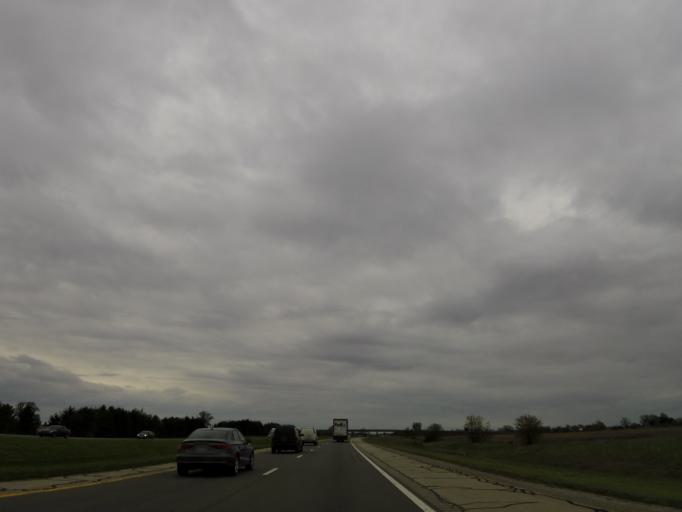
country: US
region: Ohio
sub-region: Madison County
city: Bethel
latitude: 39.7227
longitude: -83.3946
